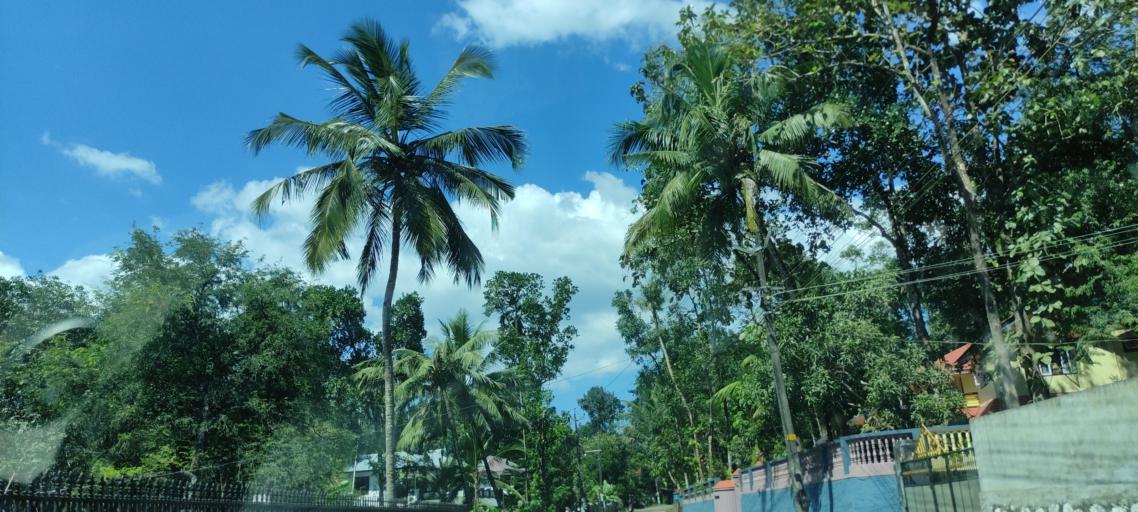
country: IN
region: Kerala
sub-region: Pattanamtitta
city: Adur
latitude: 9.1056
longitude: 76.6882
